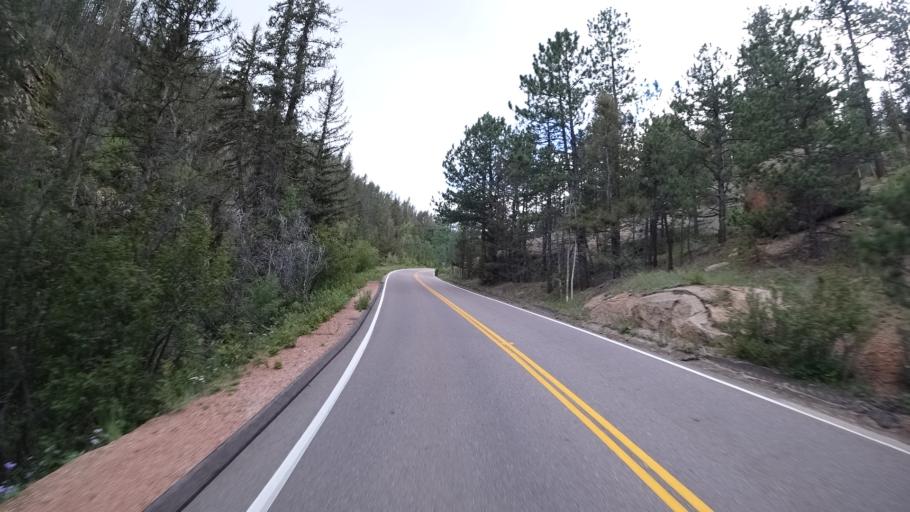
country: US
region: Colorado
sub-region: El Paso County
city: Cascade-Chipita Park
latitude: 38.9003
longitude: -104.9892
